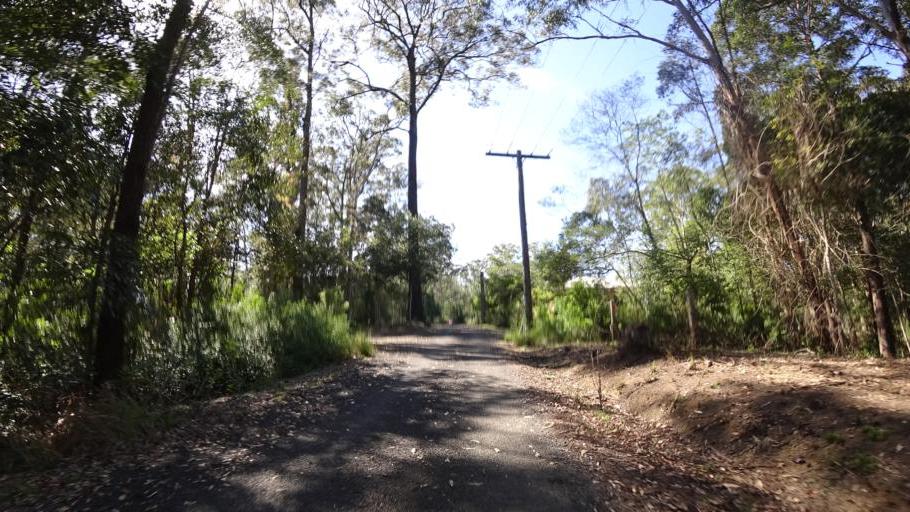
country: AU
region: Queensland
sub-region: Moreton Bay
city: Highvale
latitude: -27.4021
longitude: 152.7836
